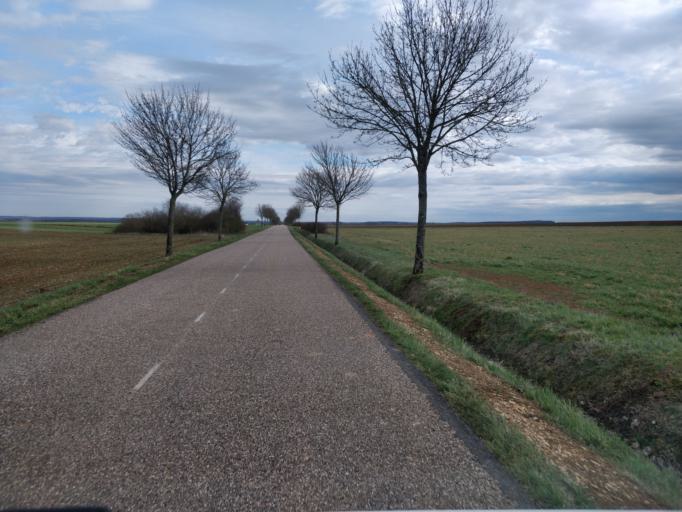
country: FR
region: Lorraine
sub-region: Departement de Meurthe-et-Moselle
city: Doncourt-les-Conflans
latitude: 49.1136
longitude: 5.9046
